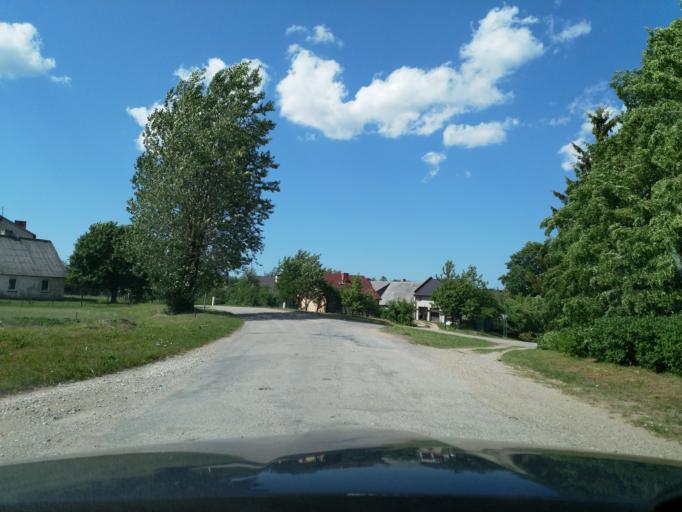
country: LV
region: Alsunga
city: Alsunga
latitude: 56.9747
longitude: 21.5662
